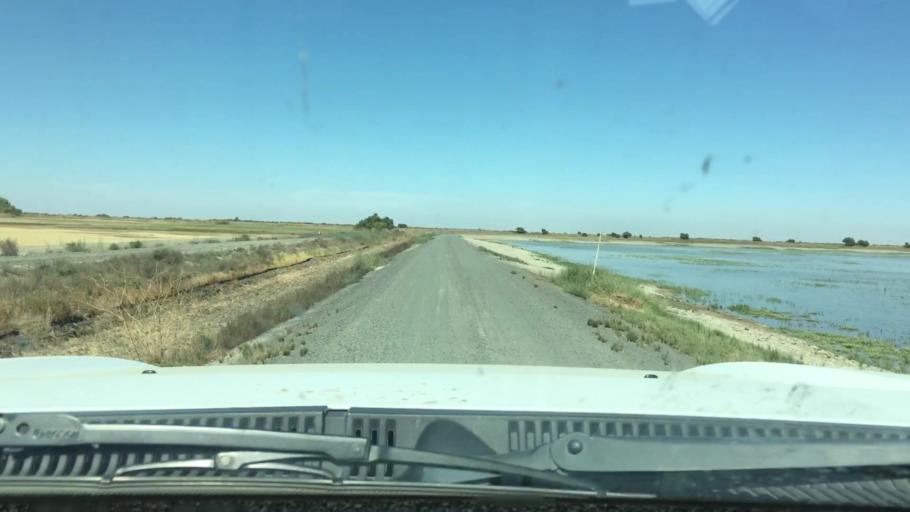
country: US
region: California
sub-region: Kern County
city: Lost Hills
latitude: 35.7353
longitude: -119.6097
